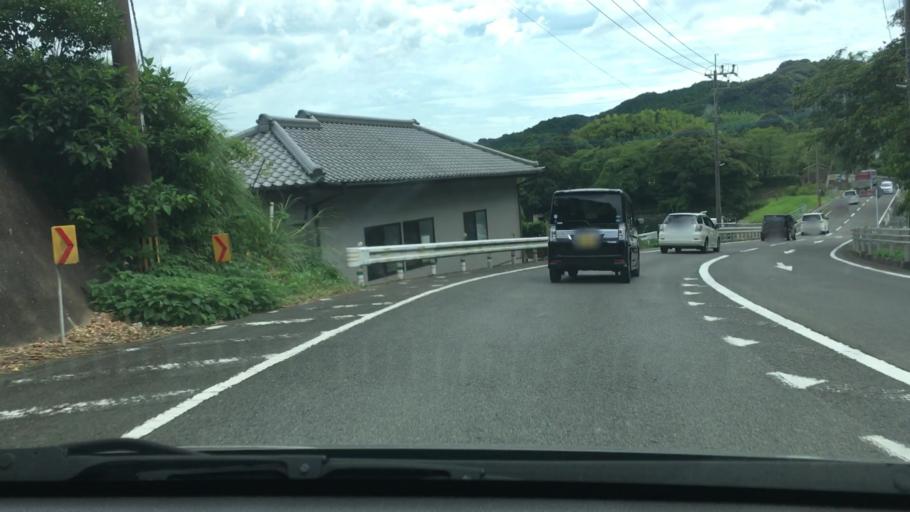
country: JP
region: Nagasaki
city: Togitsu
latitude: 32.9364
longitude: 129.7841
